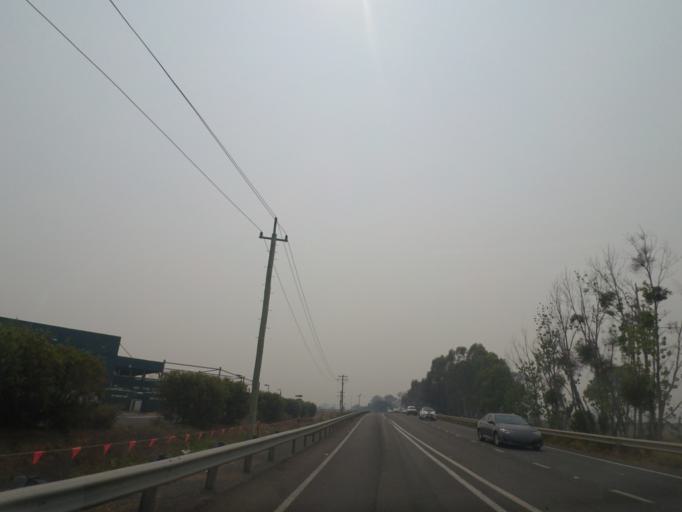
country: AU
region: New South Wales
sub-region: Clarence Valley
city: South Grafton
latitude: -29.7067
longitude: 152.9442
